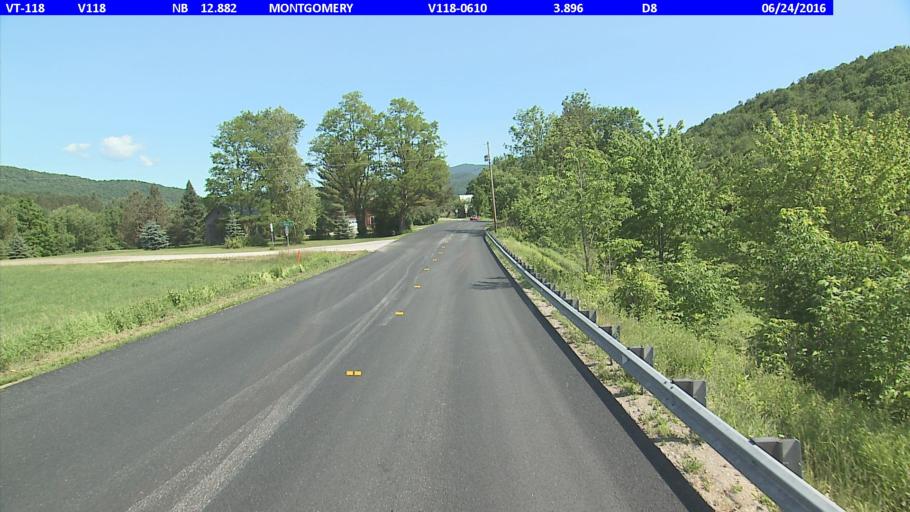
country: US
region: Vermont
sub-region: Franklin County
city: Richford
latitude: 44.8538
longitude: -72.6110
